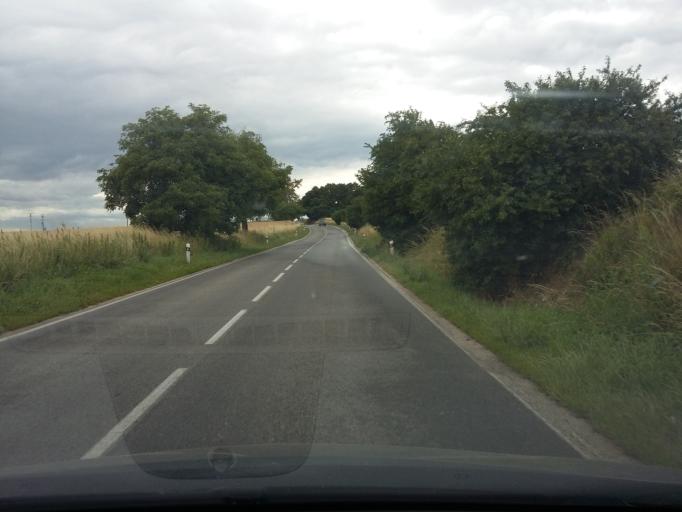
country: SK
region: Trnavsky
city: Vrbove
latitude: 48.5737
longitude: 17.6357
